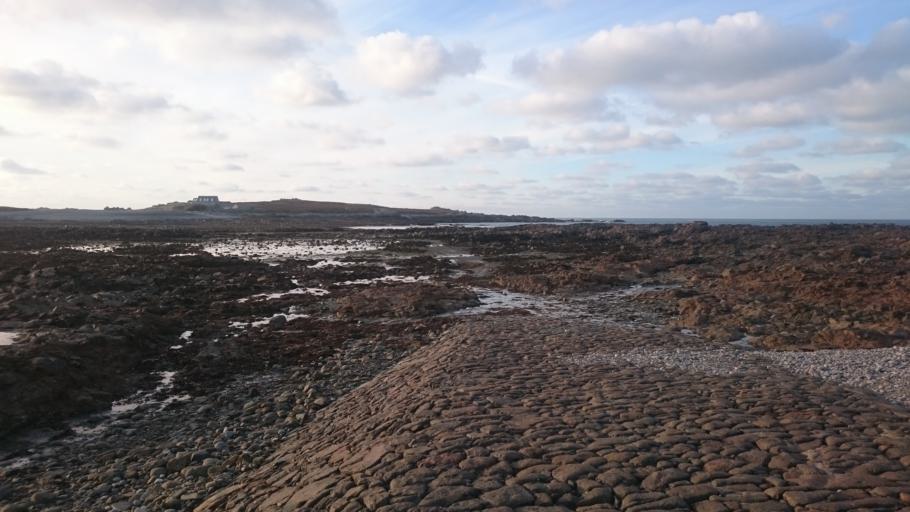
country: GG
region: St Peter Port
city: Saint Peter Port
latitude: 49.4576
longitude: -2.6582
